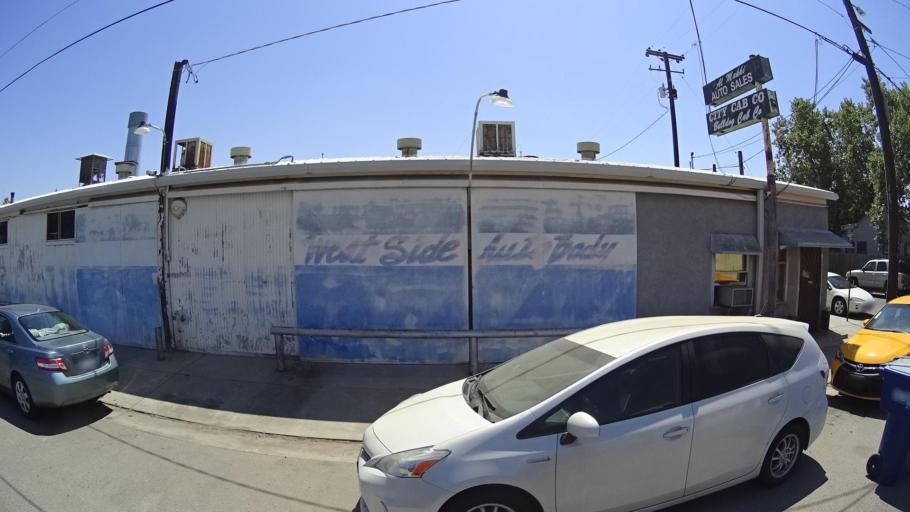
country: US
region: California
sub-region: Fresno County
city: Fresno
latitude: 36.7605
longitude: -119.7894
